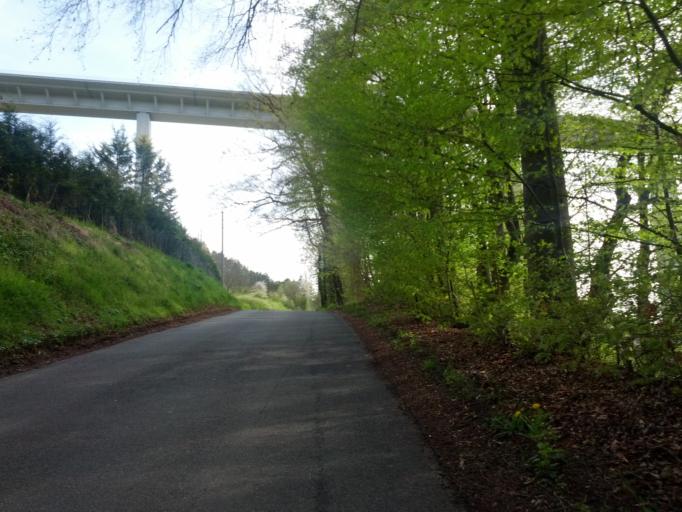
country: DE
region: Thuringia
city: Krauthausen
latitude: 51.0117
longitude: 10.2341
